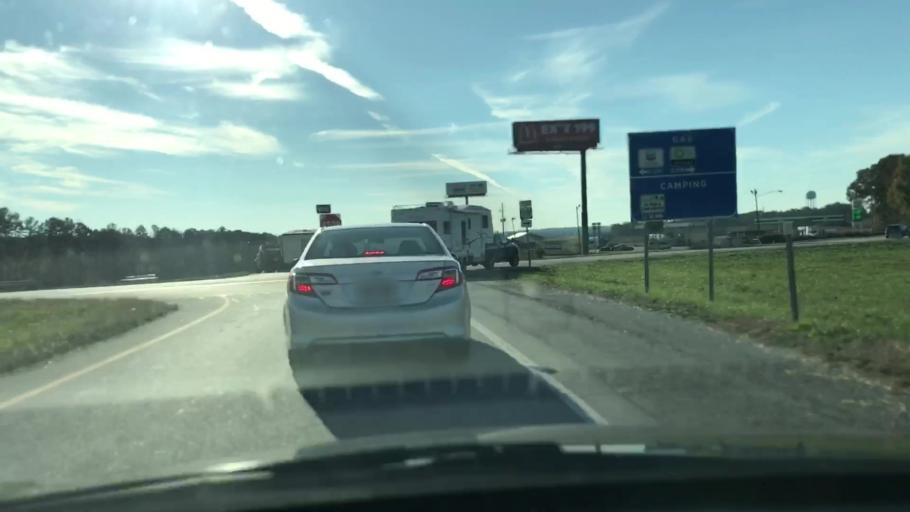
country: US
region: Alabama
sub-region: Cleburne County
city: Heflin
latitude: 33.6466
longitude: -85.5037
